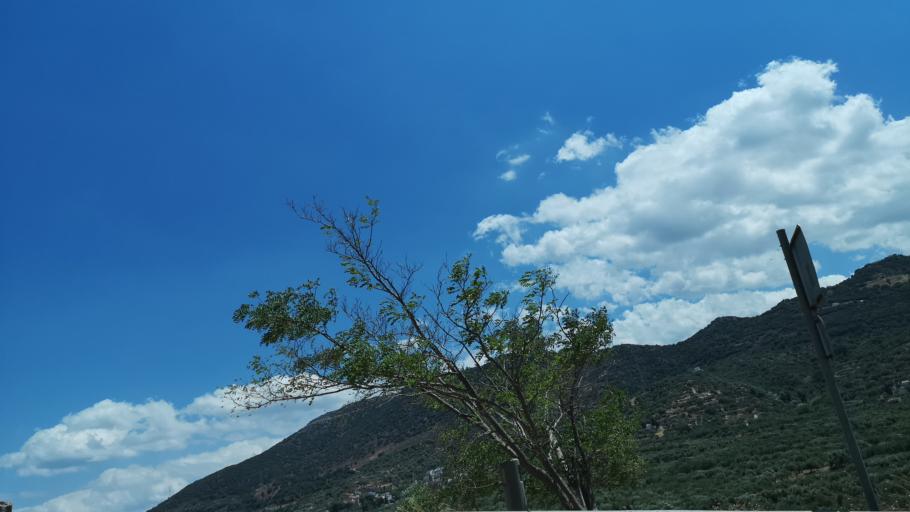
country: GR
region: Crete
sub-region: Nomos Lasithiou
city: Neapoli
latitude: 35.2498
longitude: 25.6252
